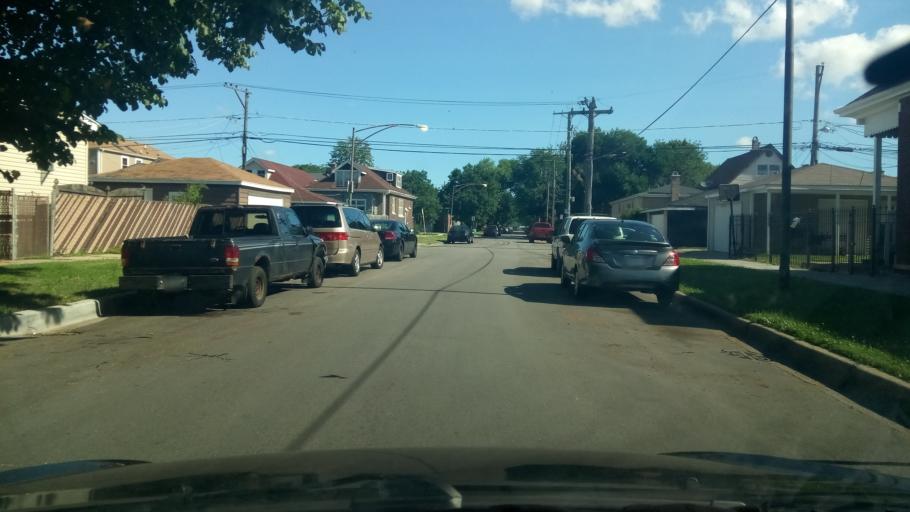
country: US
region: Illinois
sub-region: Cook County
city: Hometown
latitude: 41.7815
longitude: -87.7180
